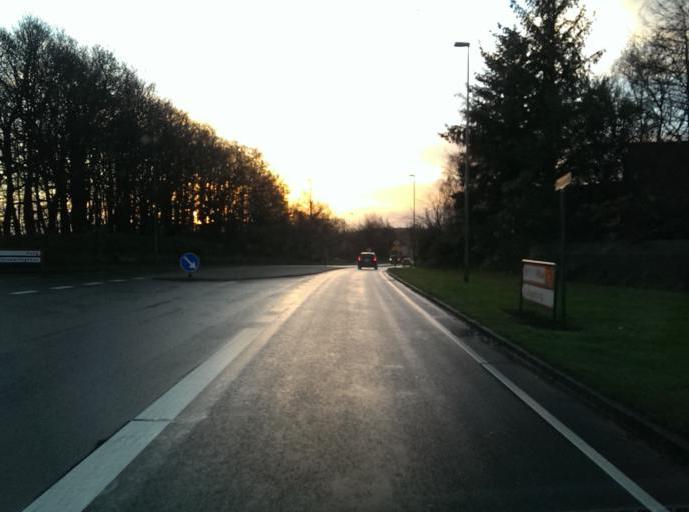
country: DK
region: South Denmark
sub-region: Esbjerg Kommune
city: Bramming
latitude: 55.4870
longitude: 8.6408
